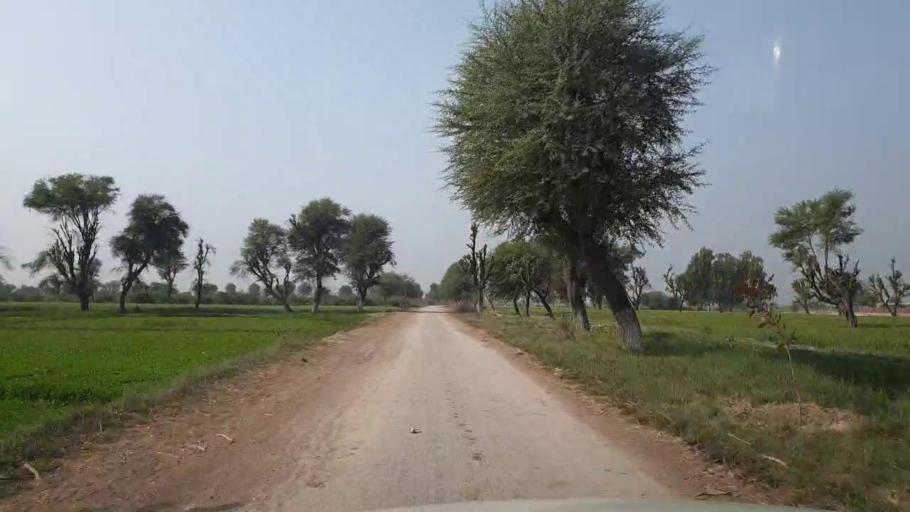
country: PK
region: Sindh
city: Umarkot
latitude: 25.4345
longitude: 69.7163
